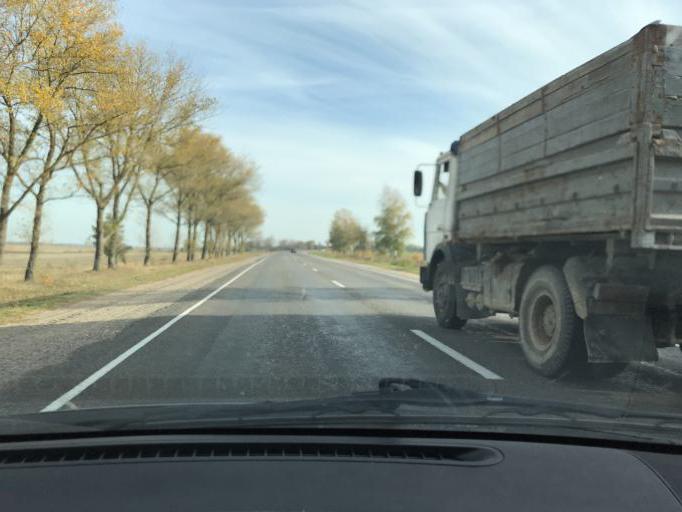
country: BY
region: Brest
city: Lahishyn
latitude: 52.2412
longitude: 26.0004
